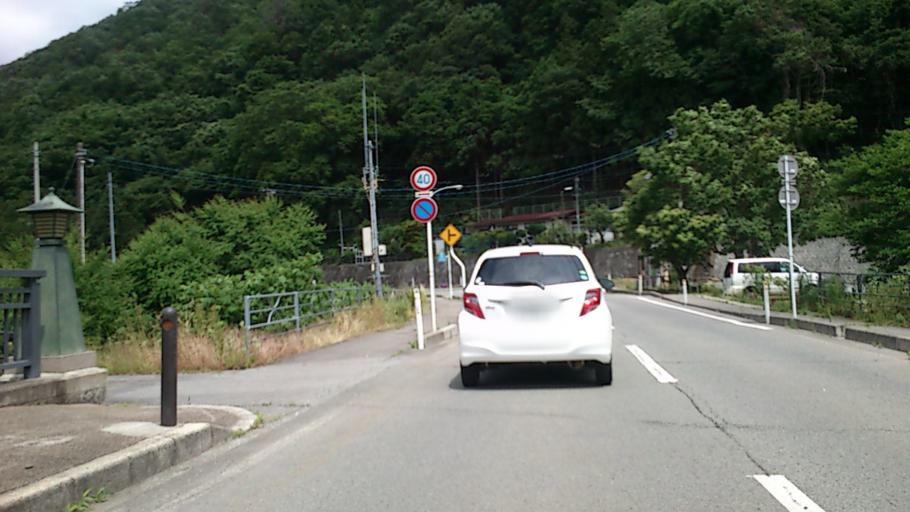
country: JP
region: Yamagata
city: Tendo
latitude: 38.3105
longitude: 140.4310
